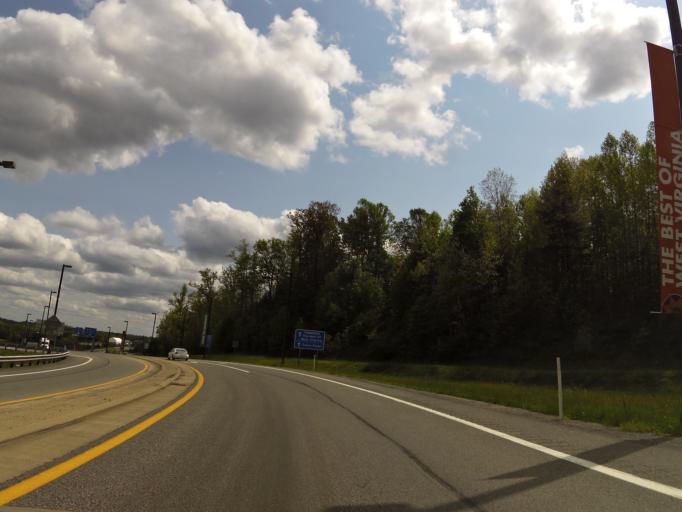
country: US
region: West Virginia
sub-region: Raleigh County
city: Prosperity
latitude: 37.8107
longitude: -81.2147
